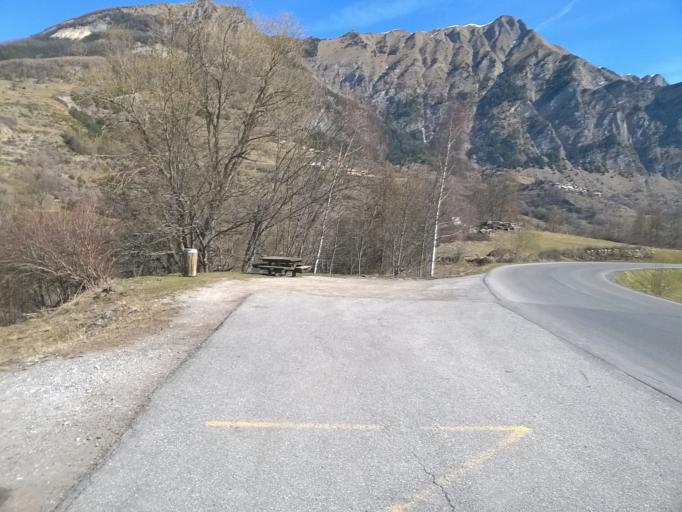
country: FR
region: Provence-Alpes-Cote d'Azur
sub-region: Departement des Hautes-Alpes
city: Embrun
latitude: 44.5083
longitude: 6.5587
